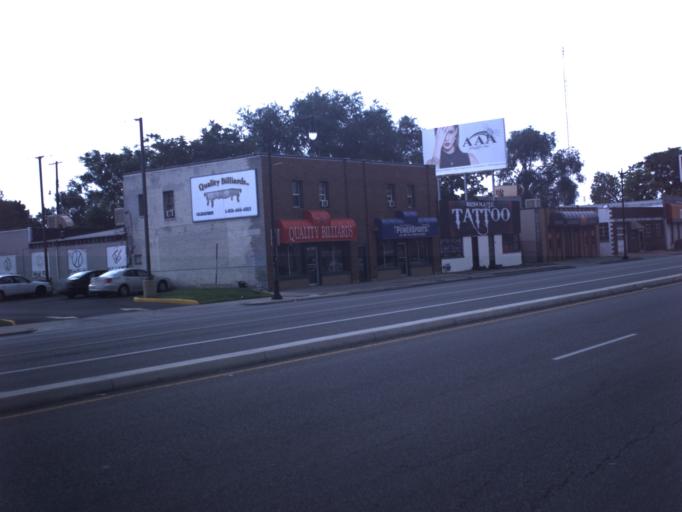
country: US
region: Utah
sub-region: Salt Lake County
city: South Salt Lake
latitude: 40.7337
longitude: -111.8881
